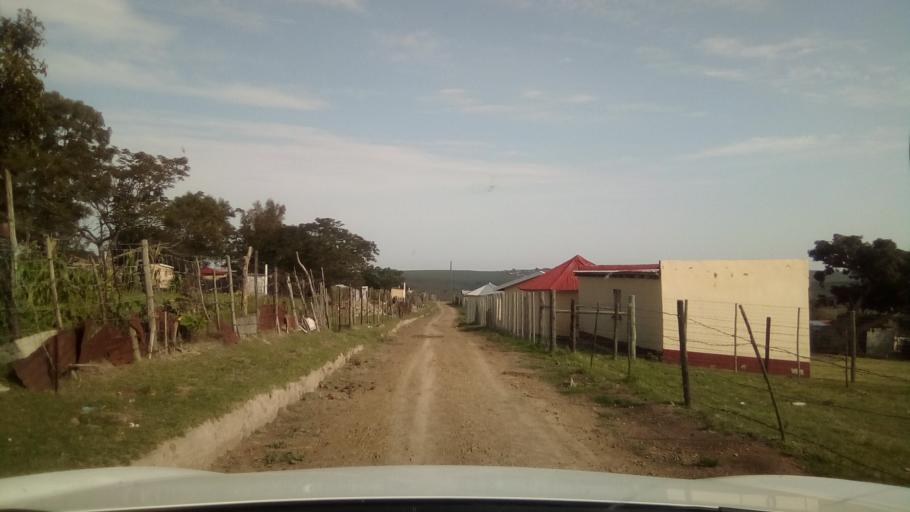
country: ZA
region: Eastern Cape
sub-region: Buffalo City Metropolitan Municipality
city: Bhisho
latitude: -33.0045
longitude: 27.3011
